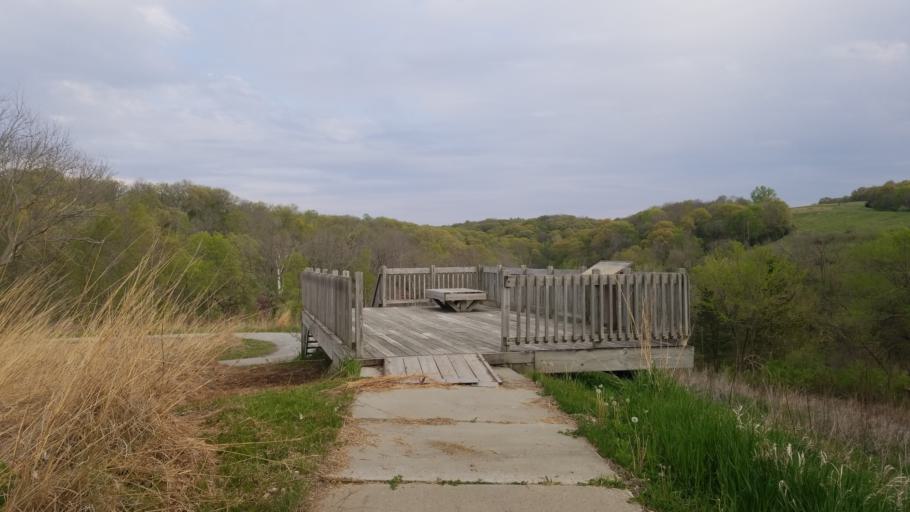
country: US
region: Iowa
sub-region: Mills County
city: Glenwood
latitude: 41.0472
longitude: -95.7830
